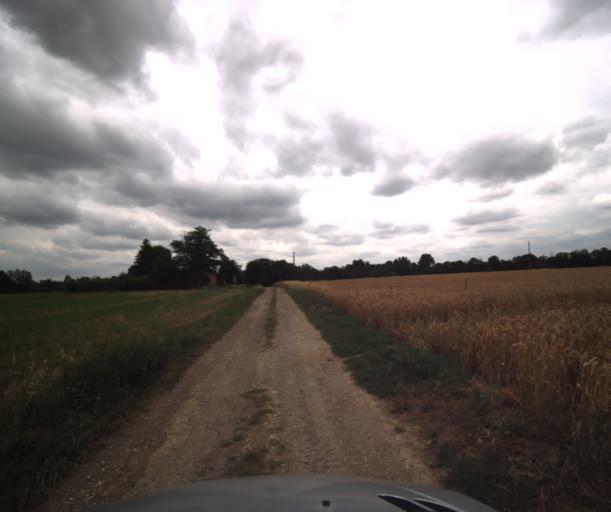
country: FR
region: Midi-Pyrenees
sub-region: Departement de la Haute-Garonne
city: Labarthe-sur-Leze
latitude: 43.4424
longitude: 1.4029
